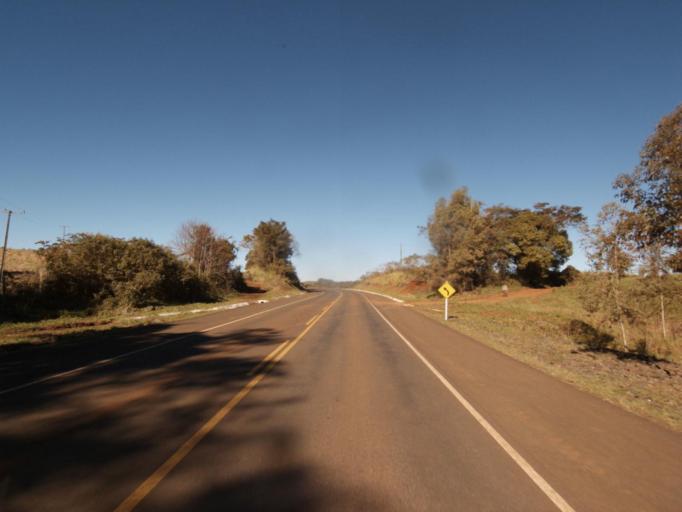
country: AR
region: Misiones
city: Bernardo de Irigoyen
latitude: -26.6710
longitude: -53.5868
